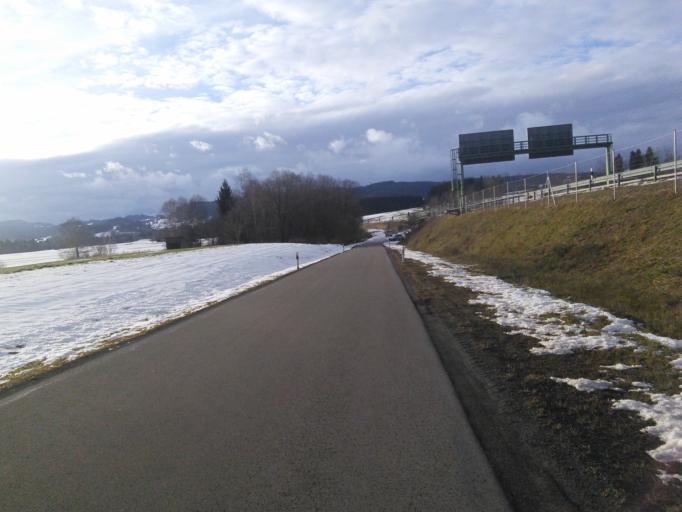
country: DE
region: Bavaria
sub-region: Swabia
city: Waltenhofen
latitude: 47.6803
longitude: 10.3025
